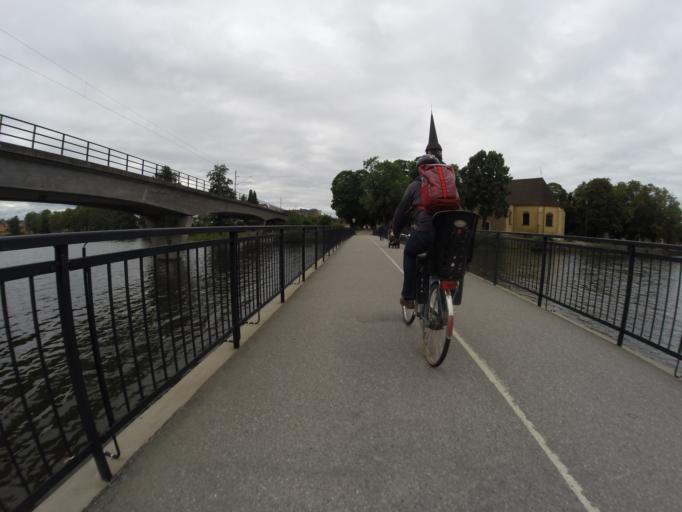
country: SE
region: Soedermanland
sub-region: Eskilstuna Kommun
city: Eskilstuna
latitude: 59.3666
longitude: 16.5176
